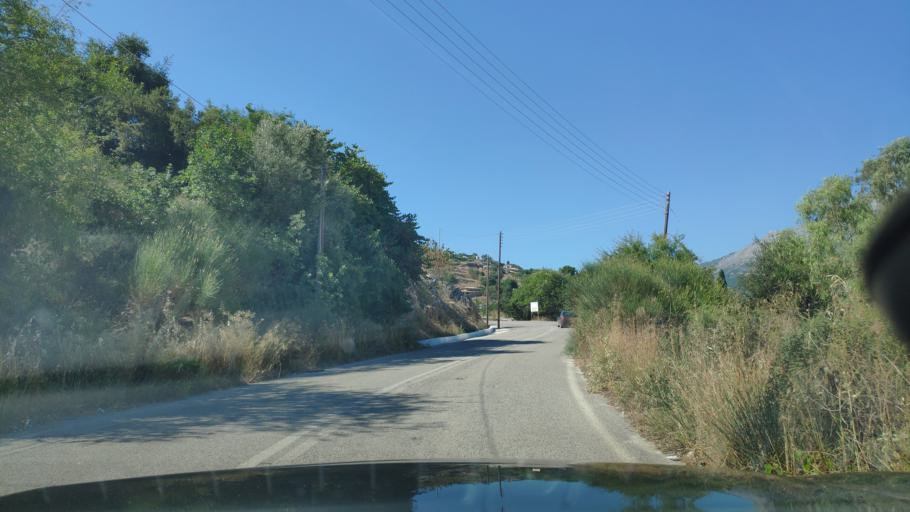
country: GR
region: Ionian Islands
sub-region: Lefkada
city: Nidri
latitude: 38.6594
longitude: 20.6007
